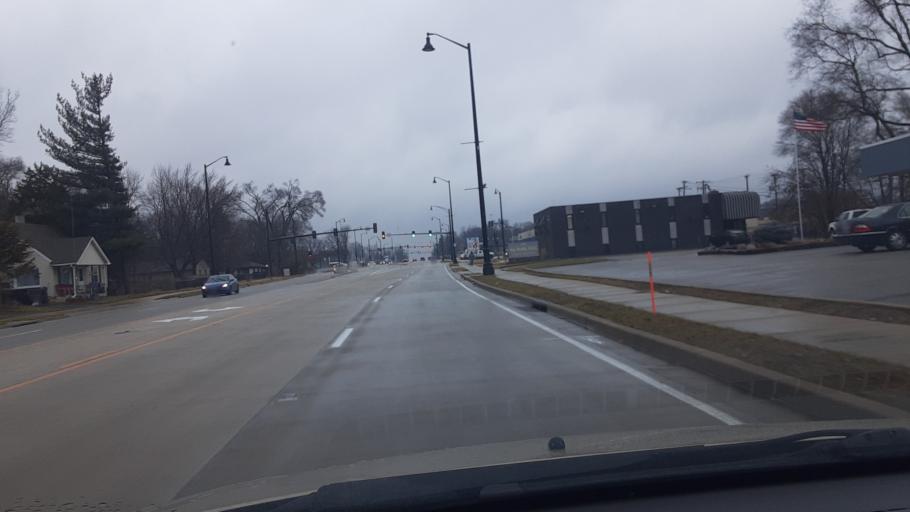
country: US
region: Illinois
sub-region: Winnebago County
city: Loves Park
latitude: 42.3127
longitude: -89.0771
